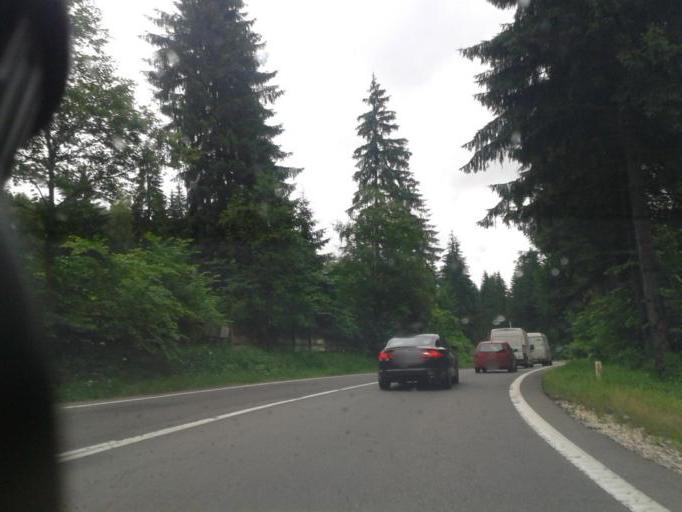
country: RO
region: Brasov
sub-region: Oras Predeal
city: Predeal
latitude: 45.5510
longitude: 25.5885
